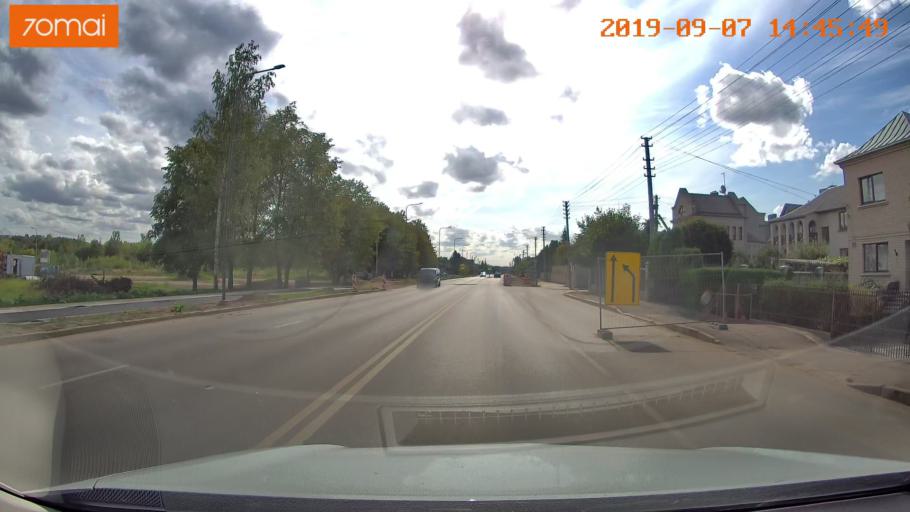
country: LT
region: Kauno apskritis
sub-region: Kaunas
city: Silainiai
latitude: 54.9303
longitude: 23.9083
